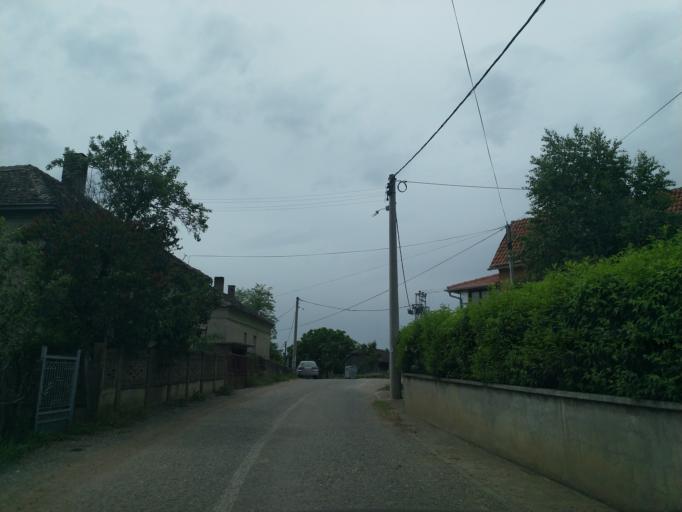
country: RS
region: Central Serbia
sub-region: Pomoravski Okrug
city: Paracin
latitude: 43.8642
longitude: 21.5826
